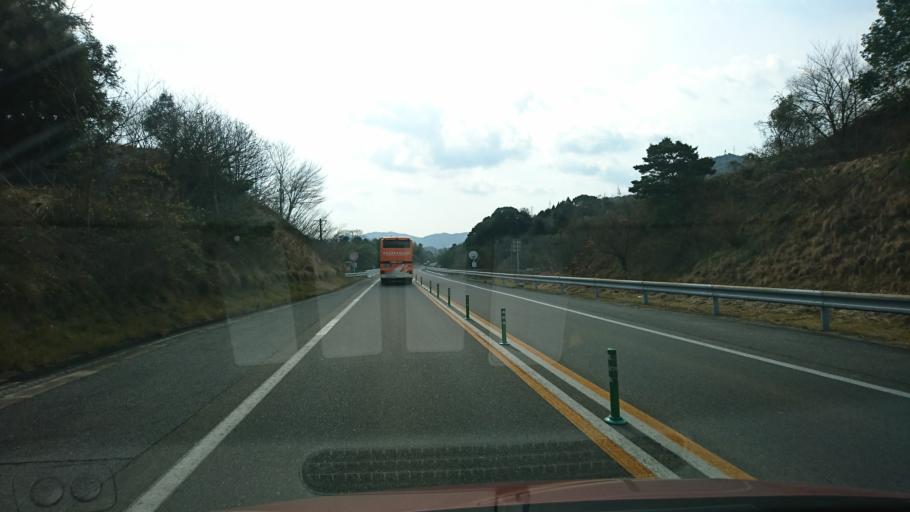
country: JP
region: Hiroshima
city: Innoshima
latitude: 34.2378
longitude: 133.0481
